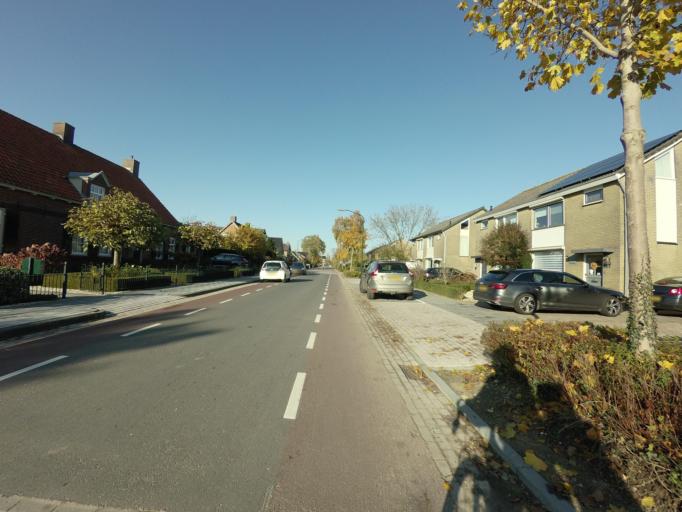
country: NL
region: North Brabant
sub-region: Gemeente Waalwijk
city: Waalwijk
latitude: 51.7311
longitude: 5.0539
